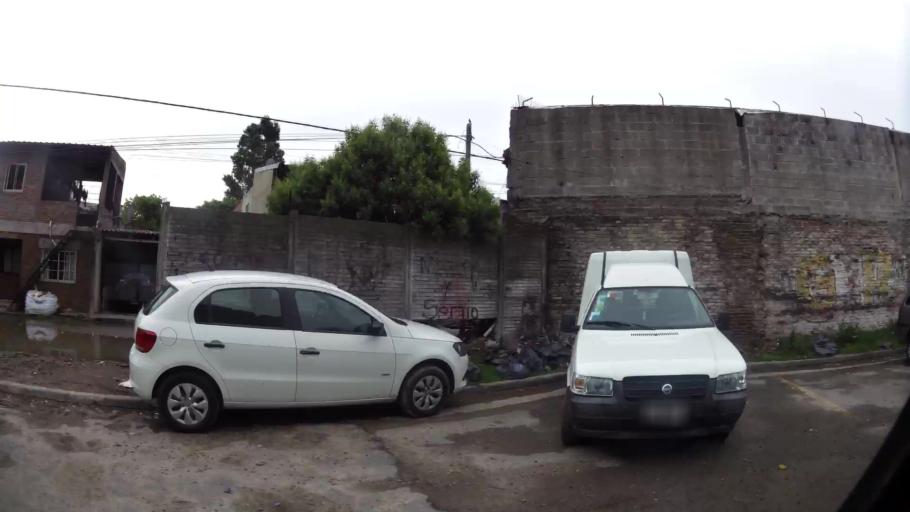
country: AR
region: Buenos Aires
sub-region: Partido de Lanus
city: Lanus
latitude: -34.7079
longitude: -58.3574
